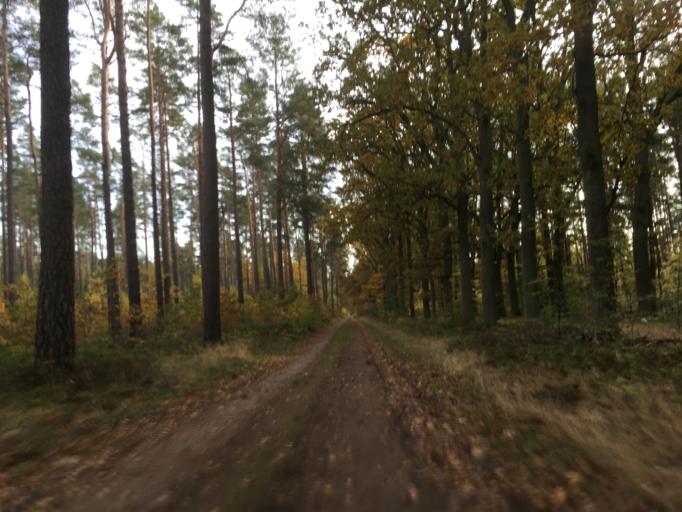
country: DE
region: Brandenburg
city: Liebenwalde
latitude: 52.9472
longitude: 13.4954
